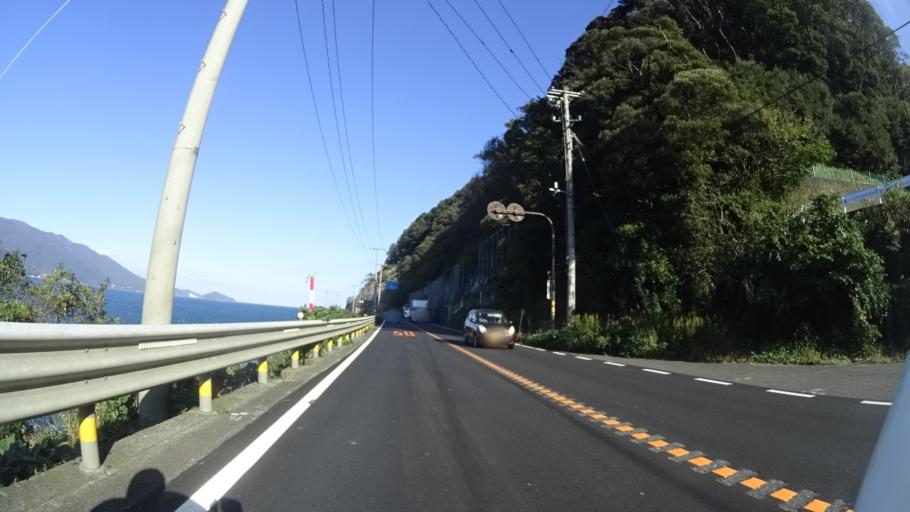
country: JP
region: Fukui
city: Tsuruga
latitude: 35.6936
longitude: 136.0817
